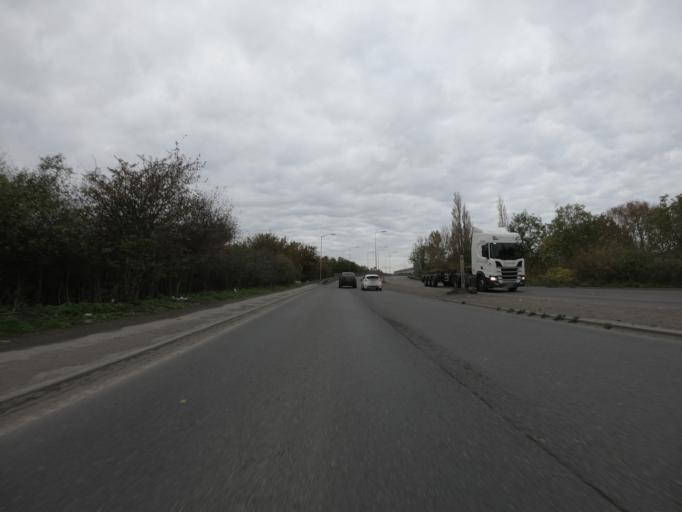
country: GB
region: England
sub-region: Borough of Thurrock
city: Tilbury
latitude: 51.4644
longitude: 0.3490
